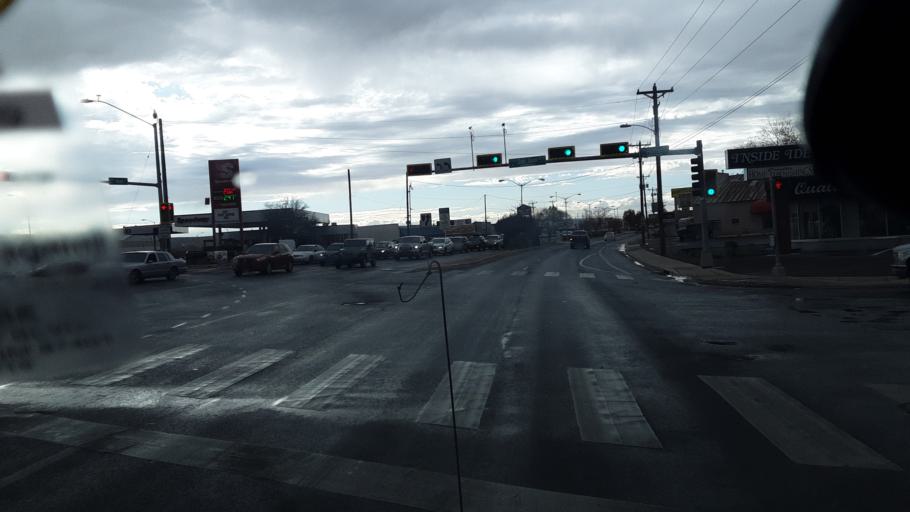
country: US
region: New Mexico
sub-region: San Juan County
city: Farmington
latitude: 36.7412
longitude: -108.1707
